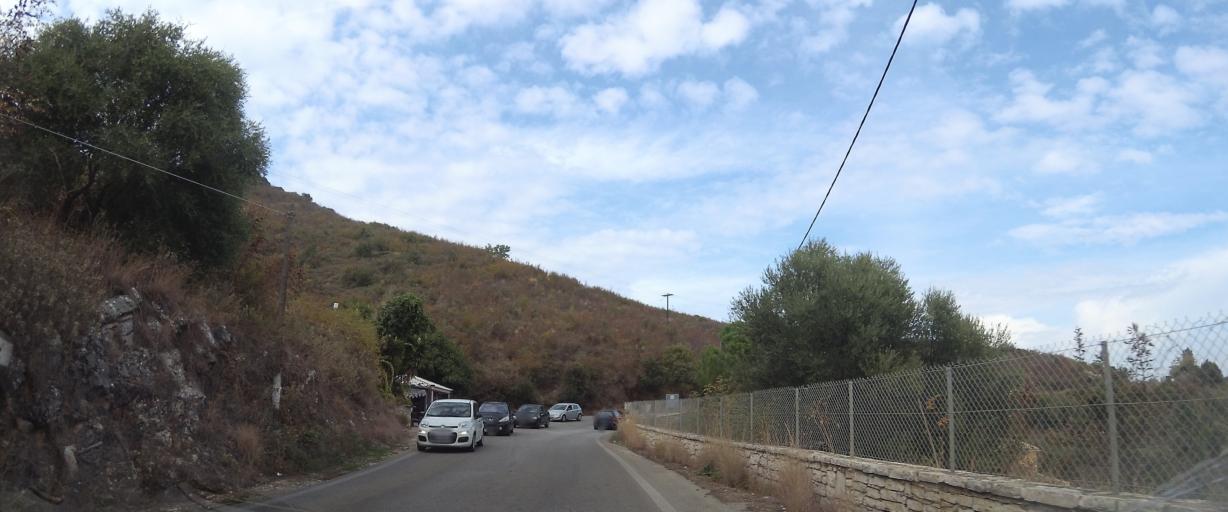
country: AL
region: Vlore
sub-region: Rrethi i Sarandes
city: Xarre
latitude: 39.7467
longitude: 19.9363
